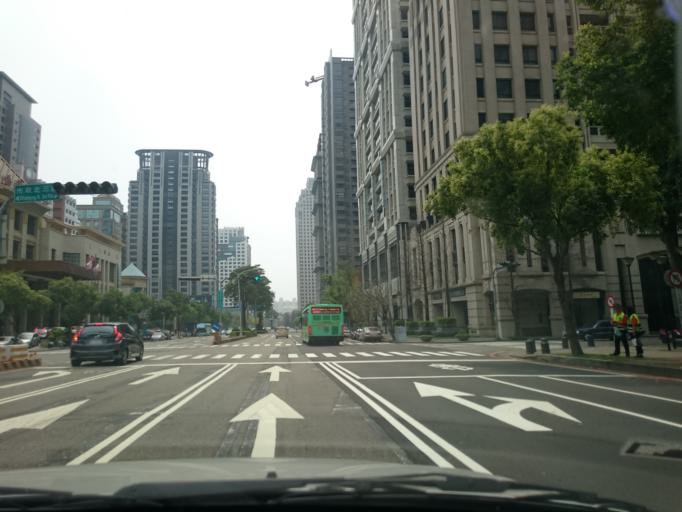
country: TW
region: Taiwan
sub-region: Taichung City
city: Taichung
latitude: 24.1609
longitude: 120.6440
